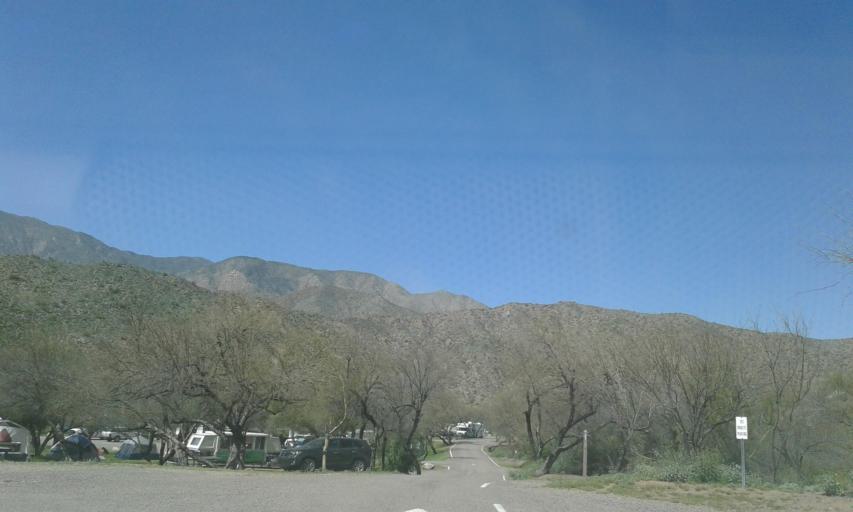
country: US
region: Arizona
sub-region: Gila County
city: Tonto Basin
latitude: 33.6271
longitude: -111.2053
